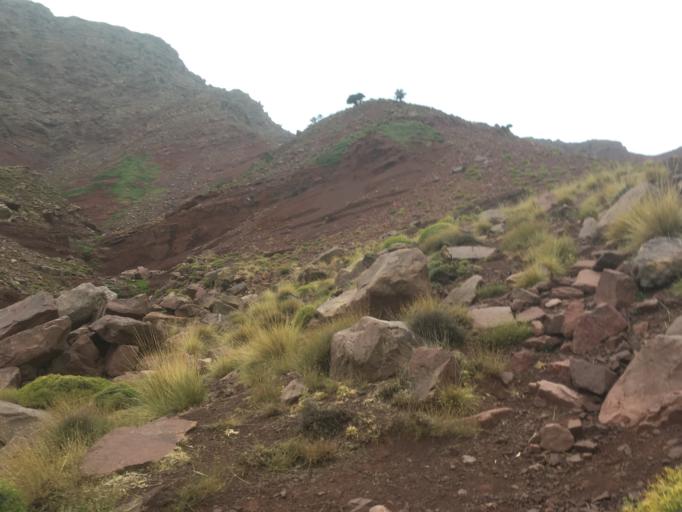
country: MA
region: Marrakech-Tensift-Al Haouz
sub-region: Al-Haouz
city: Tidili Mesfioua
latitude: 31.3284
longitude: -7.6570
